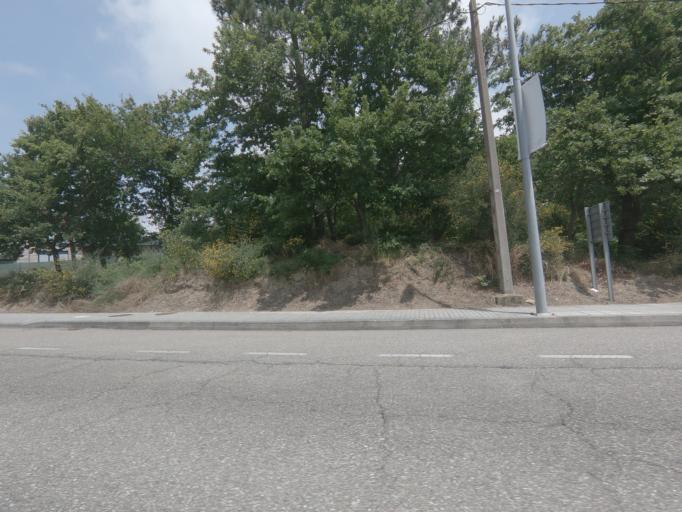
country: ES
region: Galicia
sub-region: Provincia de Pontevedra
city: A Guarda
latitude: 41.8957
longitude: -8.8582
